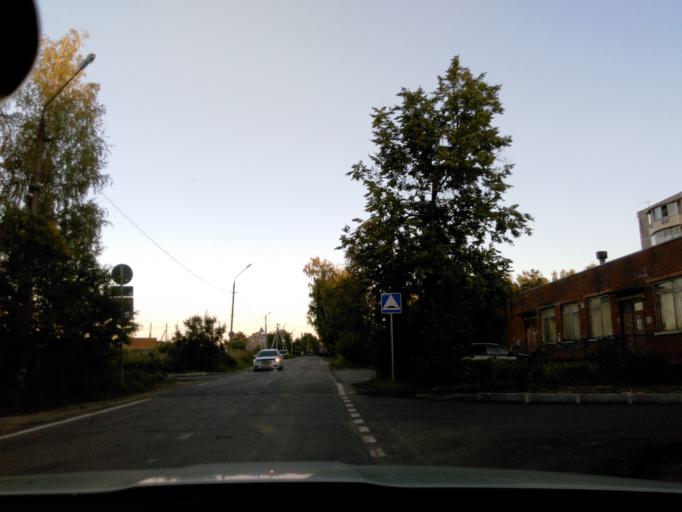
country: RU
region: Moskovskaya
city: Solnechnogorsk
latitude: 56.1270
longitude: 36.8853
